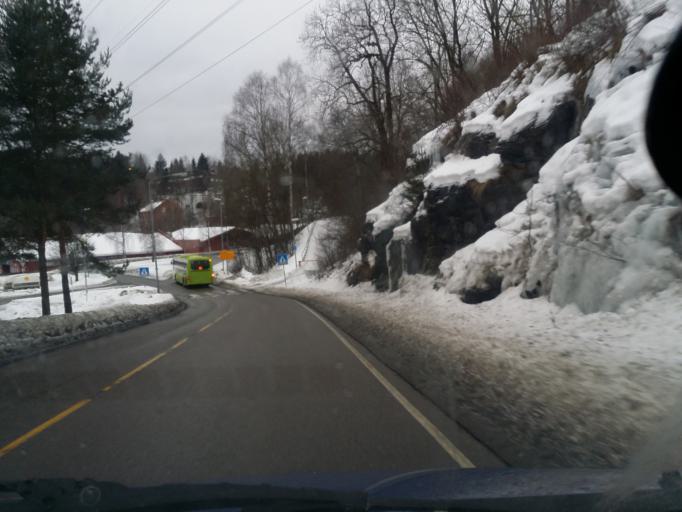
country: NO
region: Akershus
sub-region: Baerum
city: Sandvika
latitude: 59.9436
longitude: 10.5096
